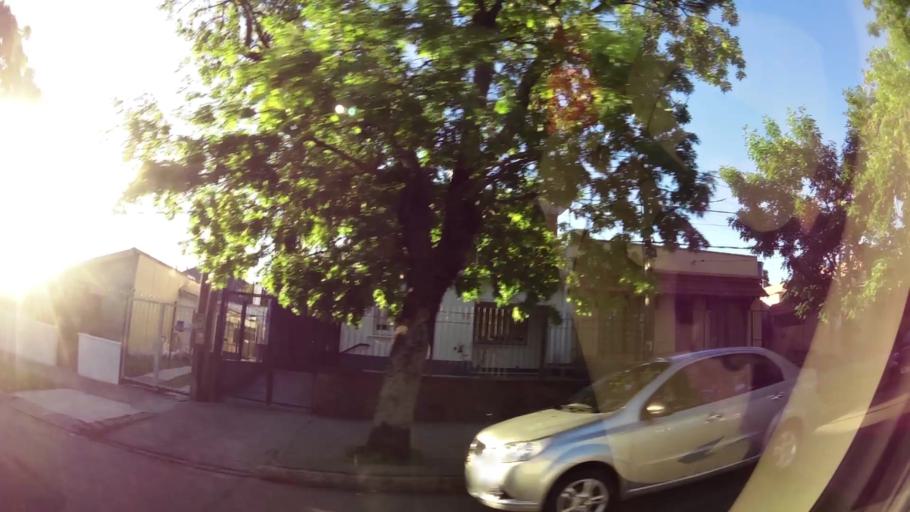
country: UY
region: Montevideo
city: Montevideo
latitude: -34.8458
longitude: -56.2082
